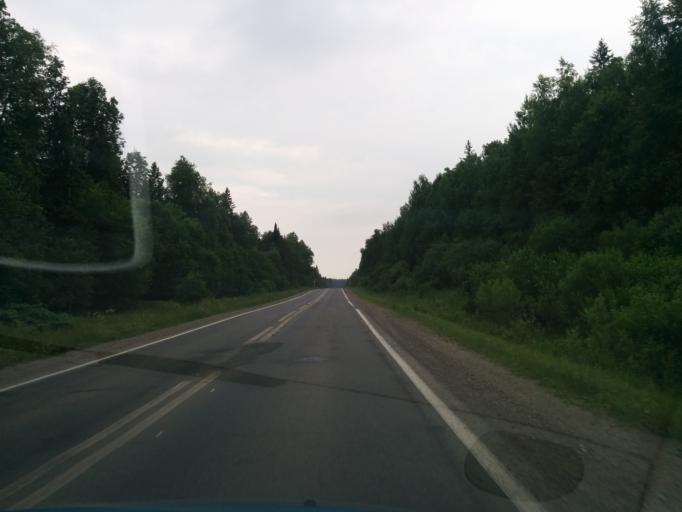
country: RU
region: Perm
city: Perm
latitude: 58.1851
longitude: 56.2206
